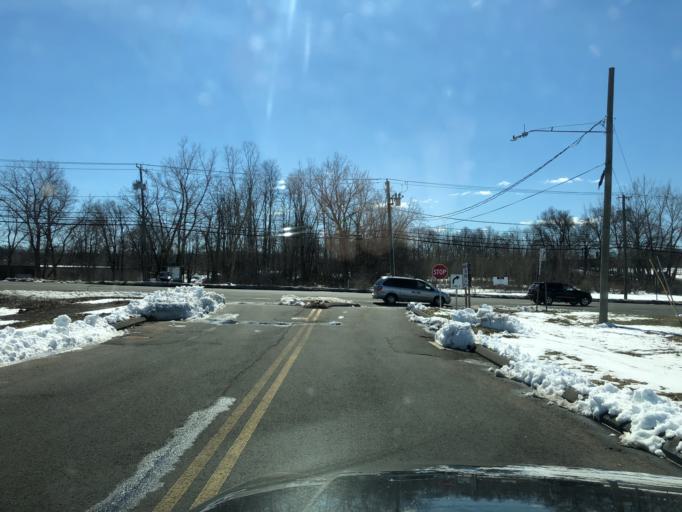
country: US
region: Connecticut
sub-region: Hartford County
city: Newington
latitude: 41.6943
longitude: -72.7562
